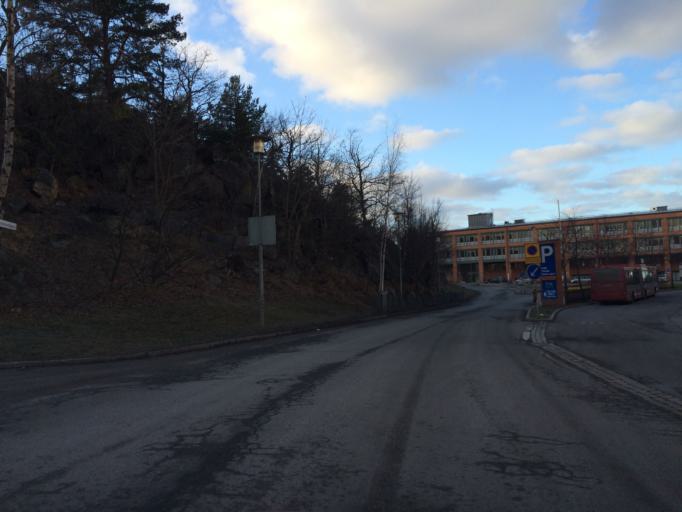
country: SE
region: Stockholm
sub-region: Nacka Kommun
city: Nacka
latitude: 59.3158
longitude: 18.1604
